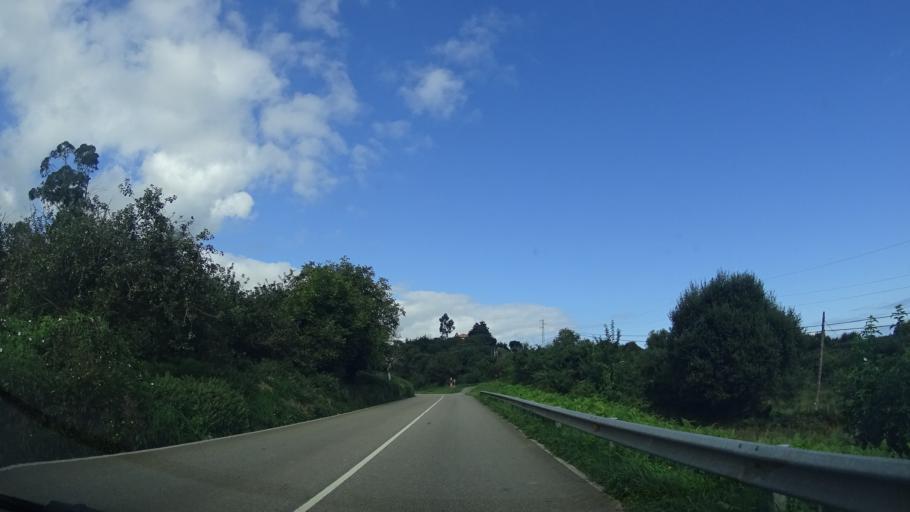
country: ES
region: Asturias
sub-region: Province of Asturias
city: Ribadesella
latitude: 43.4741
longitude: -5.1459
